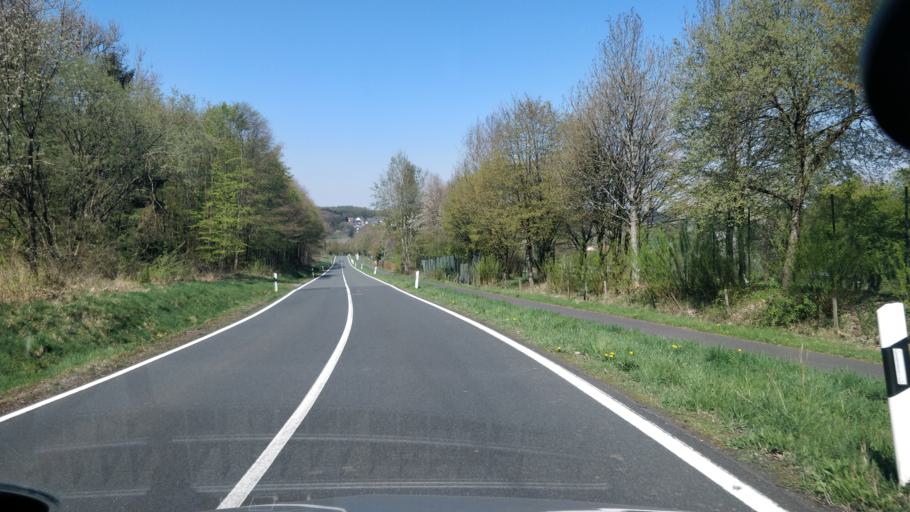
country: DE
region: Rheinland-Pfalz
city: Winnen
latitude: 50.5793
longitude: 8.0022
